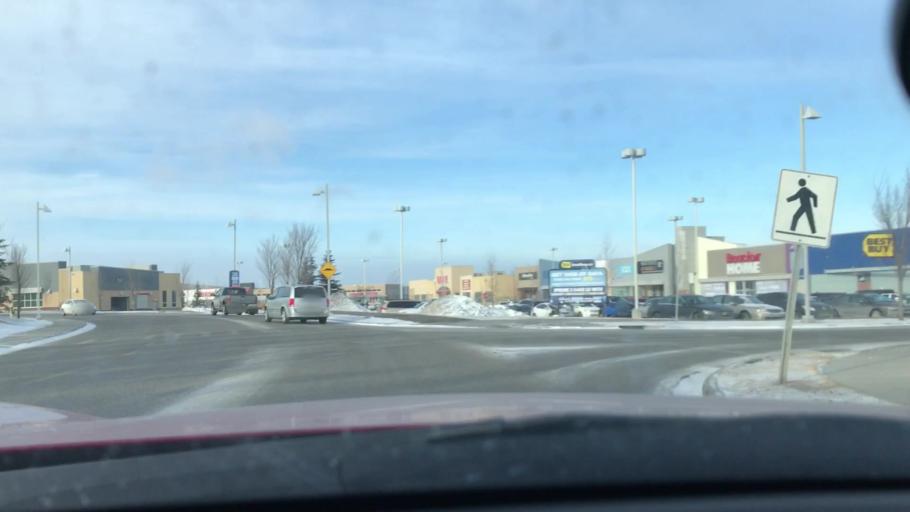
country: CA
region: Alberta
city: Calgary
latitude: 51.1567
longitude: -114.1580
